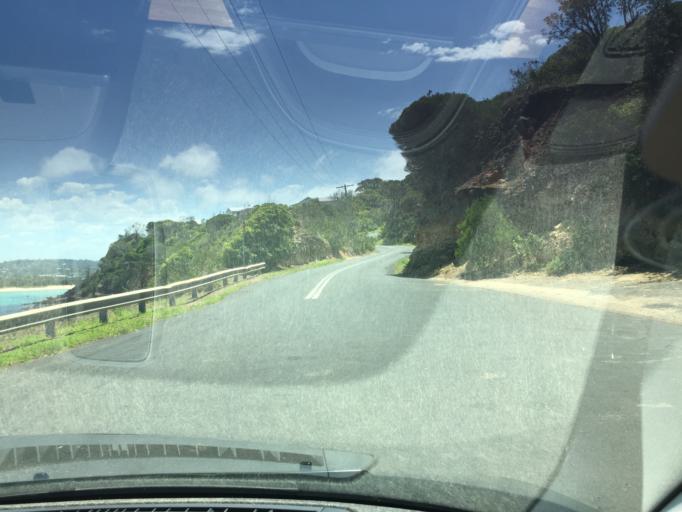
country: AU
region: New South Wales
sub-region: Bega Valley
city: Merimbula
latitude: -36.8982
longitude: 149.9274
